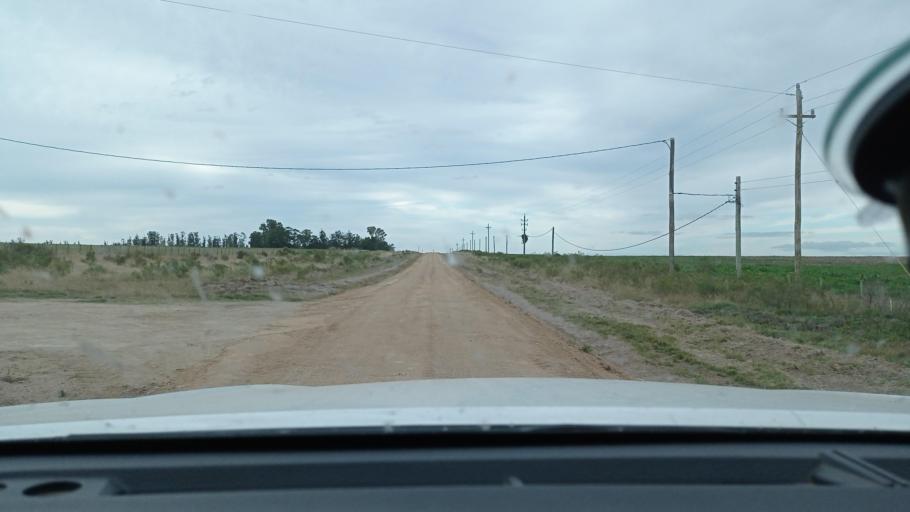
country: UY
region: Florida
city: Casupa
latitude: -34.1153
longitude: -55.7679
